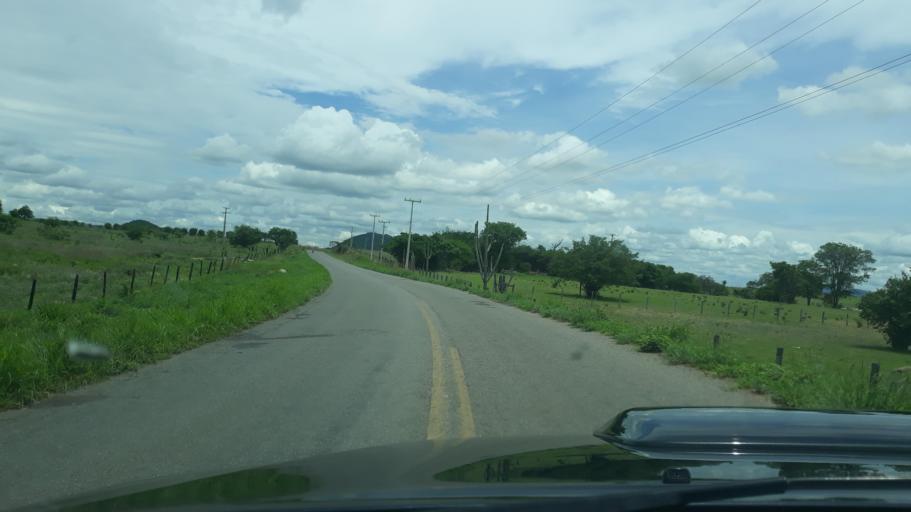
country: BR
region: Bahia
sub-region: Guanambi
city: Guanambi
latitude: -14.1525
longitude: -42.8256
